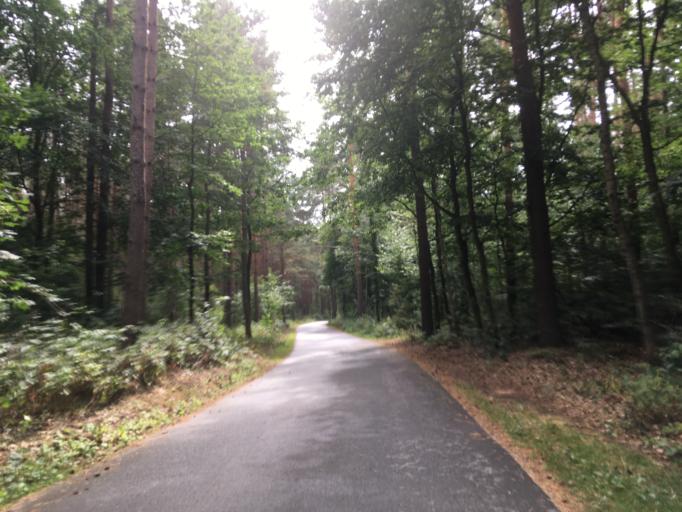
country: DE
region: Brandenburg
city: Chorin
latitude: 52.9280
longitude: 13.8603
